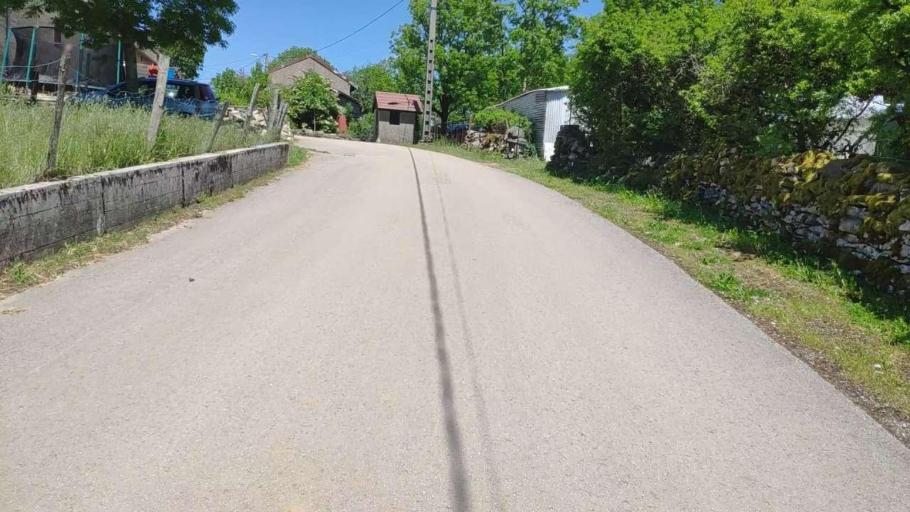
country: FR
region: Franche-Comte
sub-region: Departement du Jura
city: Poligny
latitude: 46.7361
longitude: 5.7003
